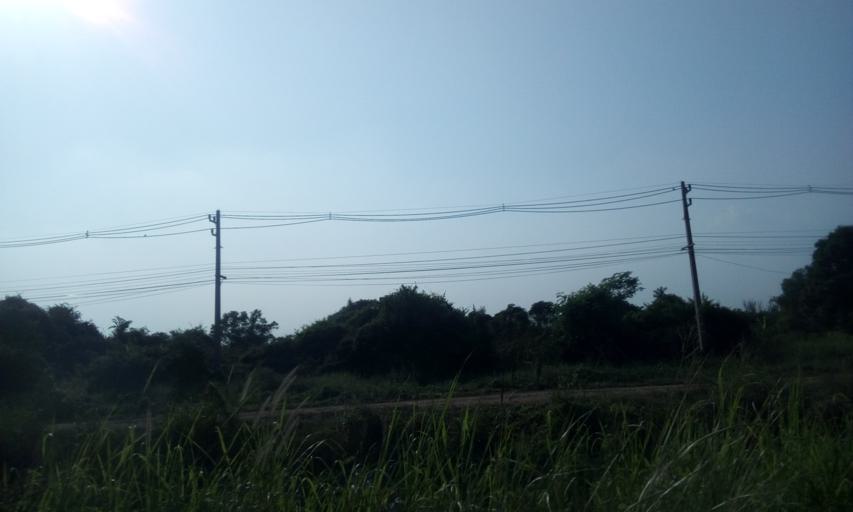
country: TH
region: Sing Buri
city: Phrom Buri
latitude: 14.8117
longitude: 100.4354
